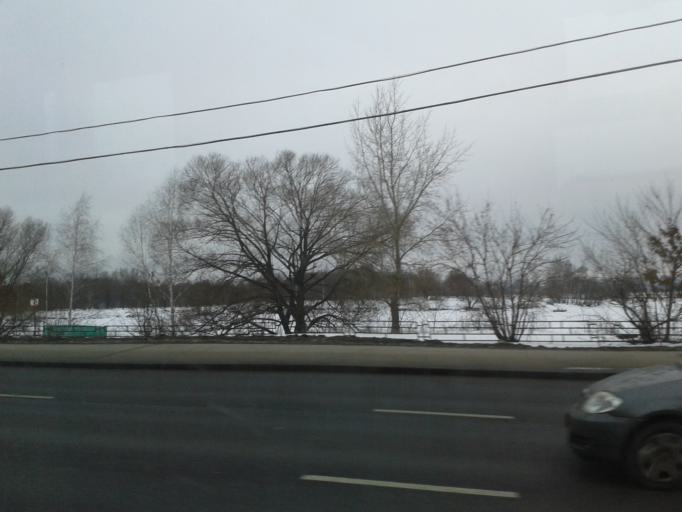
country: RU
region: Moscow
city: Shchukino
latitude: 55.8046
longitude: 37.4331
